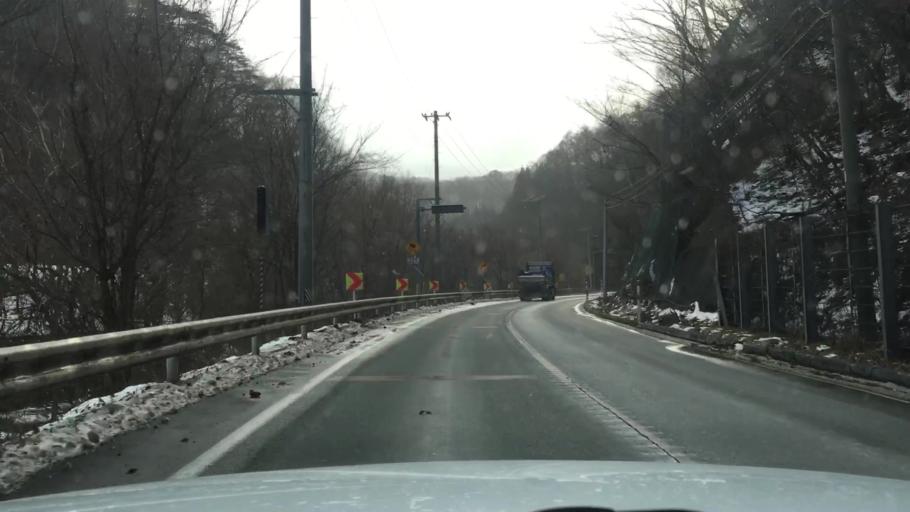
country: JP
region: Iwate
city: Tono
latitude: 39.6156
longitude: 141.4873
